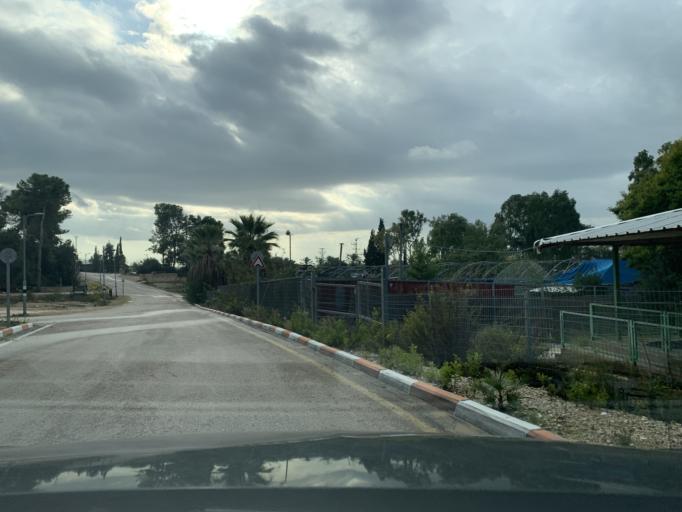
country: IL
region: Central District
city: Rosh Ha'Ayin
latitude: 32.0631
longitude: 34.9482
